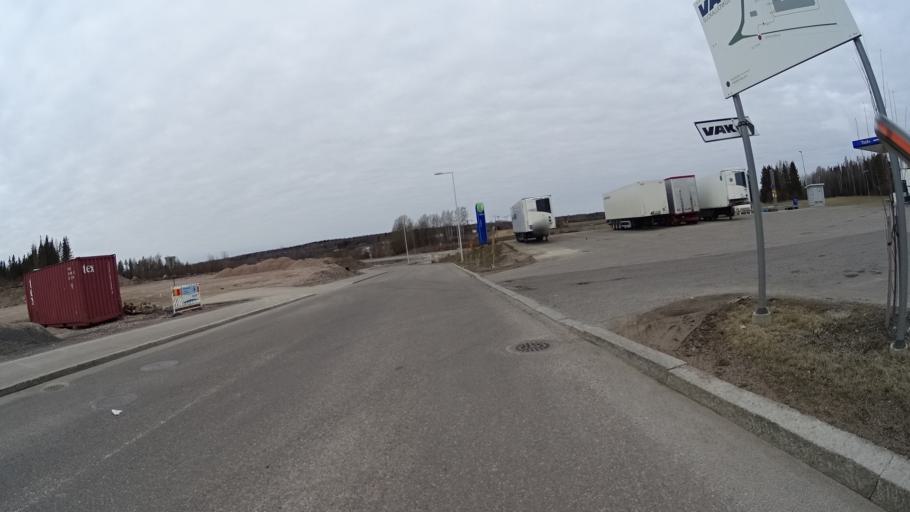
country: FI
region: Uusimaa
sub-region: Helsinki
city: Teekkarikylae
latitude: 60.3067
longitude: 24.8880
